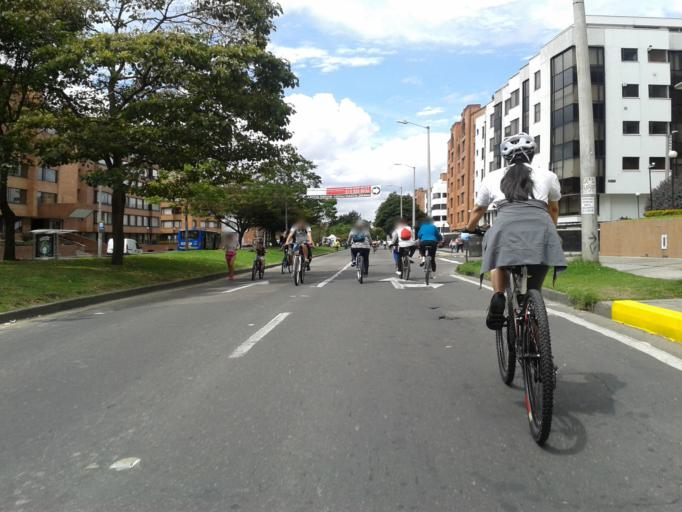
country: CO
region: Bogota D.C.
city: Barrio San Luis
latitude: 4.6953
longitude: -74.0380
